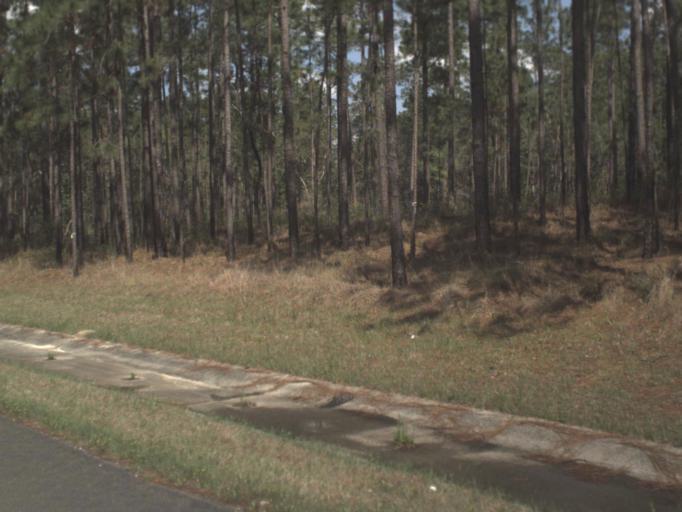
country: US
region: Florida
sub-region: Okaloosa County
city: Crestview
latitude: 30.8530
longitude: -86.8222
